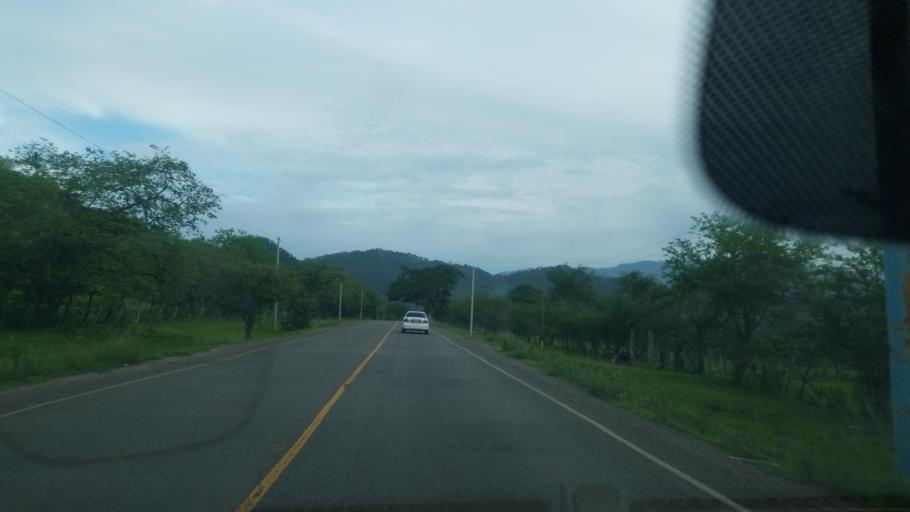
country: HN
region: Santa Barbara
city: San Vicente Centenario
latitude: 14.8696
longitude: -88.2485
